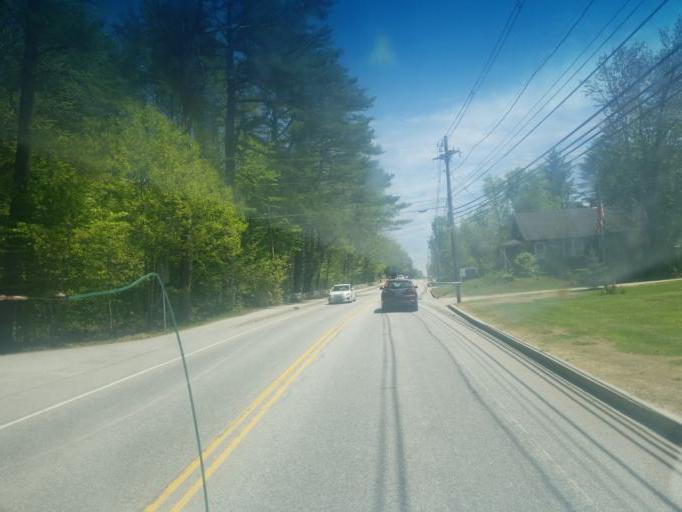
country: US
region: New Hampshire
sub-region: Grafton County
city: Plymouth
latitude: 43.7631
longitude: -71.7080
